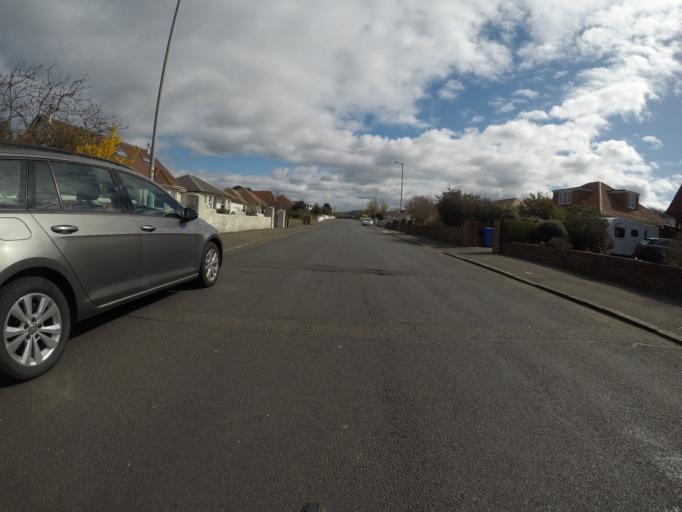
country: GB
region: Scotland
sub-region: South Ayrshire
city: Troon
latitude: 55.5614
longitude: -4.6555
